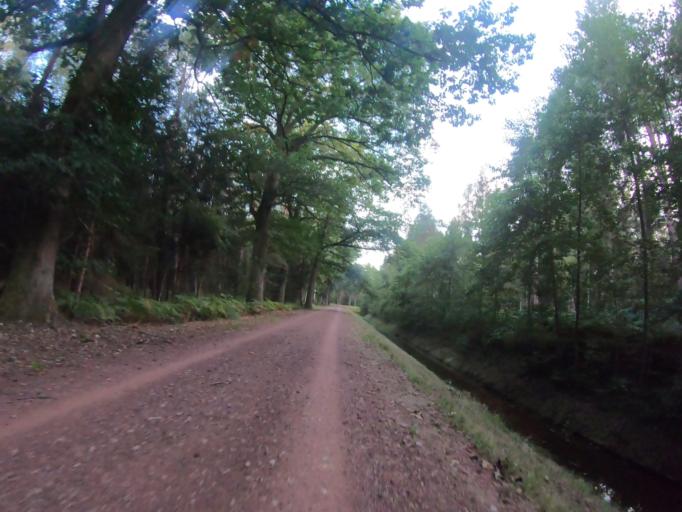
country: DE
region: Lower Saxony
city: Gifhorn
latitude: 52.5191
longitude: 10.5619
